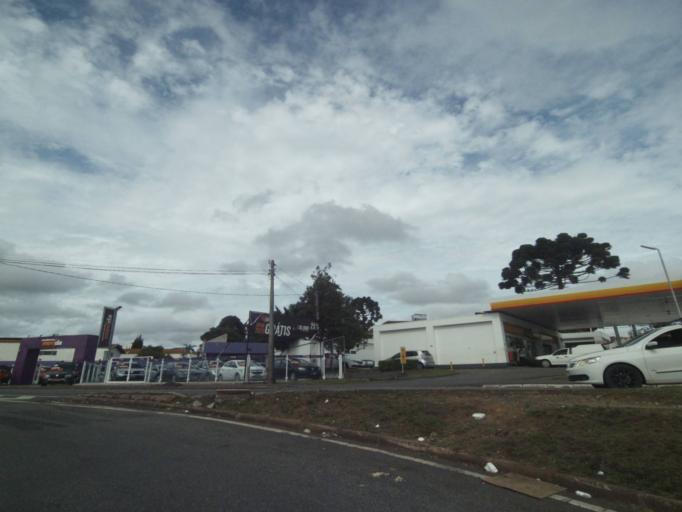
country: BR
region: Parana
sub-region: Curitiba
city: Curitiba
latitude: -25.4446
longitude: -49.3049
